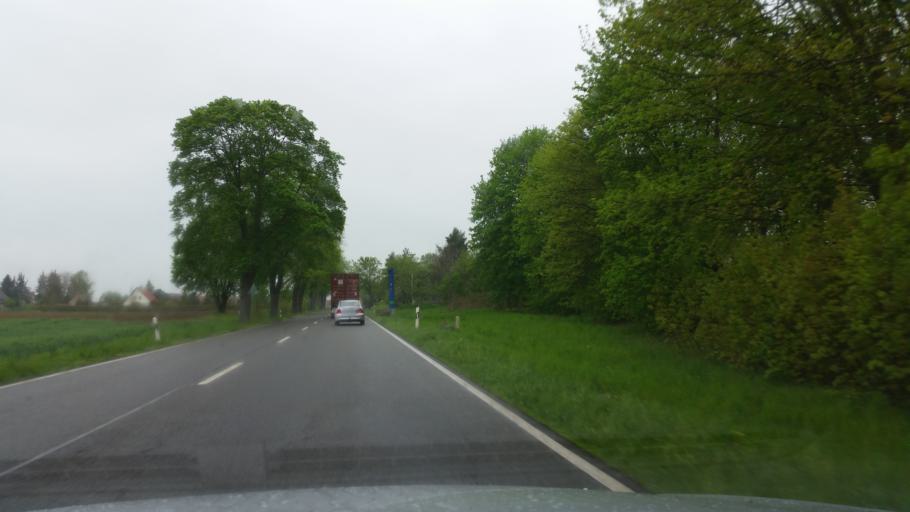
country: DE
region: Saxony-Anhalt
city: Gardelegen
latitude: 52.5697
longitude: 11.3612
